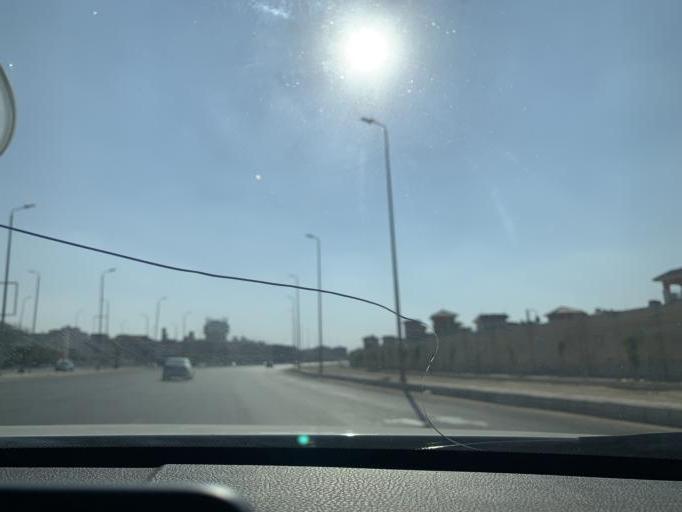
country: EG
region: Muhafazat al Qalyubiyah
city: Al Khankah
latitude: 30.0117
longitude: 31.4744
